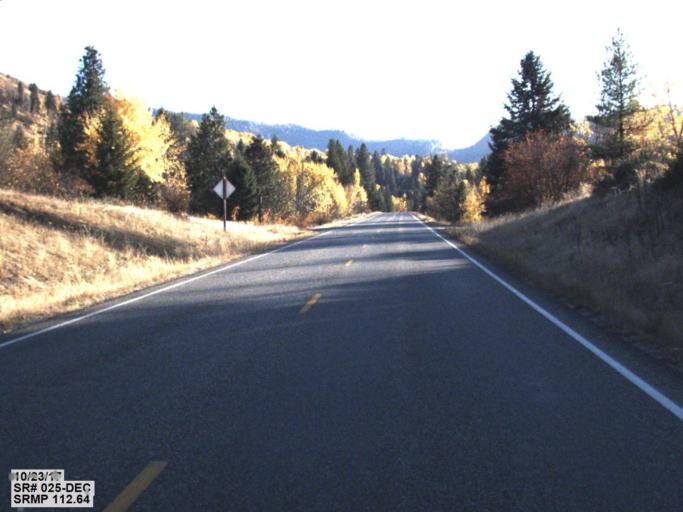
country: CA
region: British Columbia
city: Rossland
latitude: 48.9068
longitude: -117.7926
